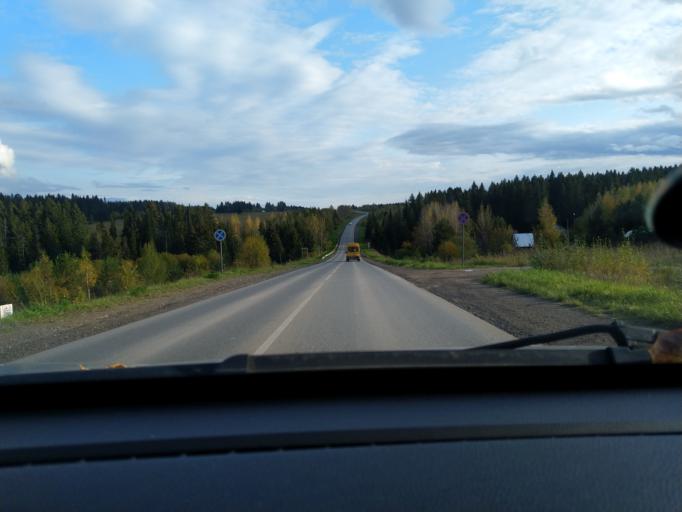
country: RU
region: Perm
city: Polazna
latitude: 58.2812
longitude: 56.4124
